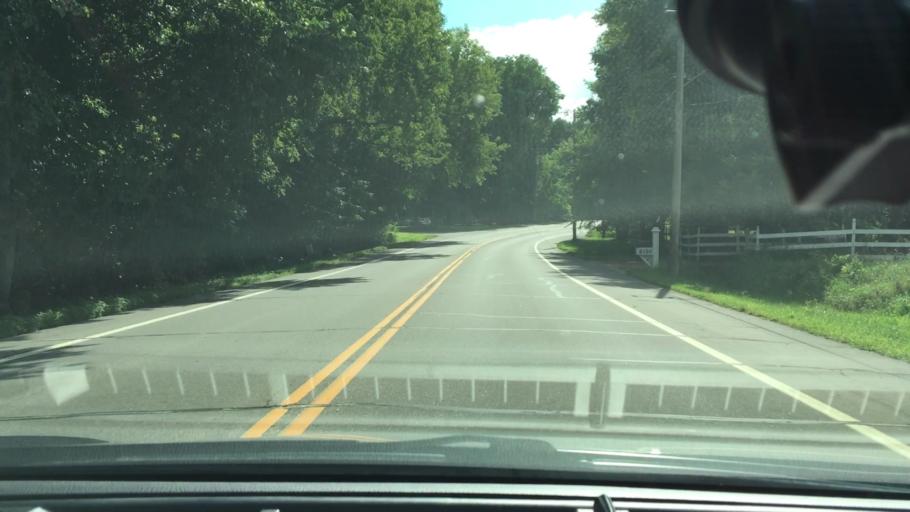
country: US
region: Minnesota
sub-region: Hennepin County
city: Minnetrista
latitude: 44.9226
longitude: -93.6954
